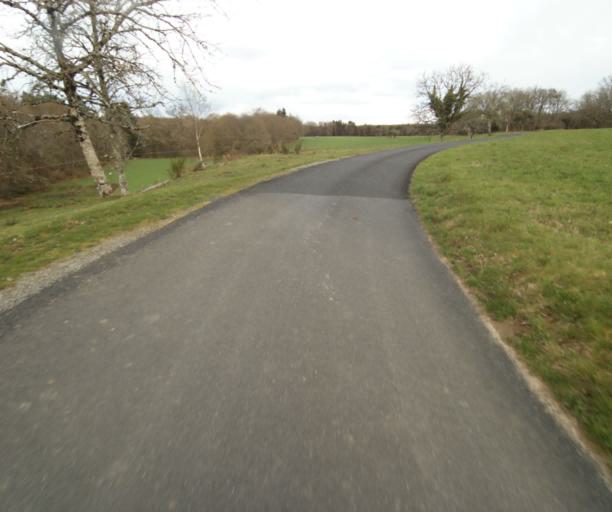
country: FR
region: Limousin
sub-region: Departement de la Correze
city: Argentat
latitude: 45.2018
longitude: 1.9933
